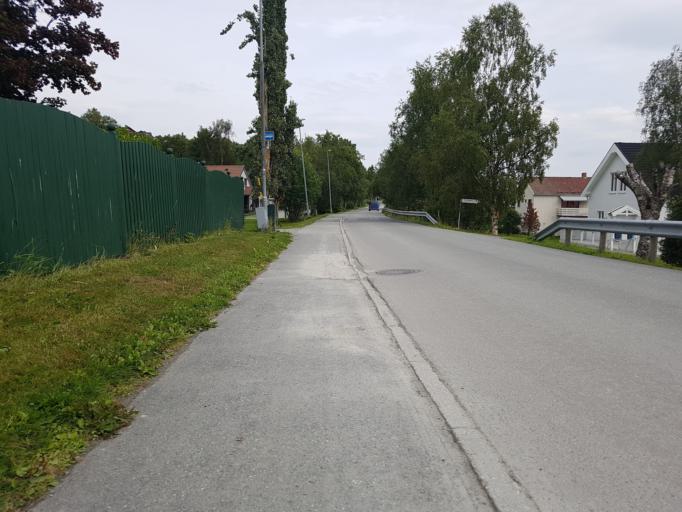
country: NO
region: Sor-Trondelag
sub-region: Trondheim
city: Trondheim
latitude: 63.3864
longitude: 10.3701
